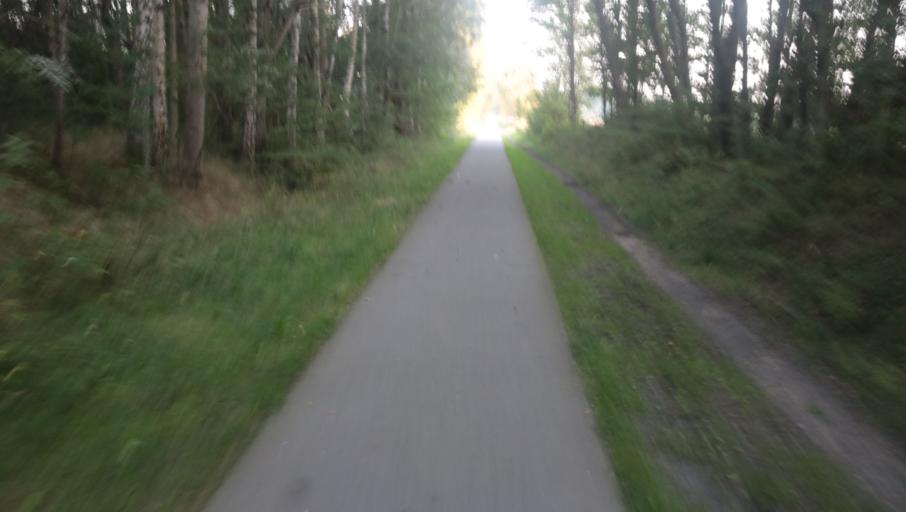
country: SE
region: Blekinge
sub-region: Karlshamns Kommun
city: Karlshamn
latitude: 56.2197
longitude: 14.8214
